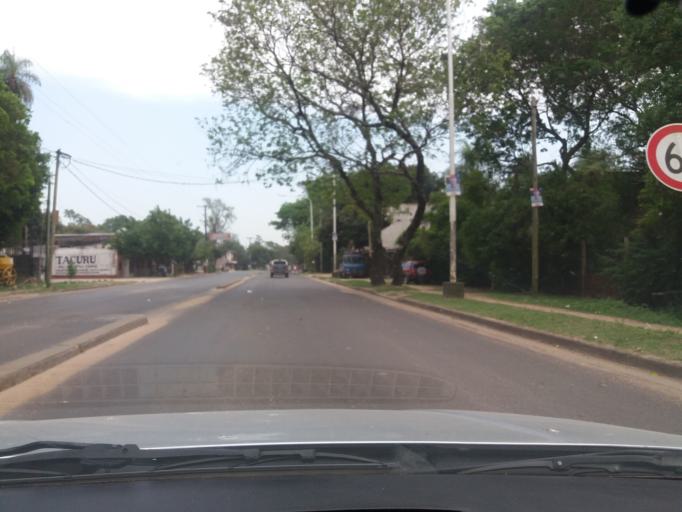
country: AR
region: Corrientes
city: Corrientes
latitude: -27.5110
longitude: -58.8097
